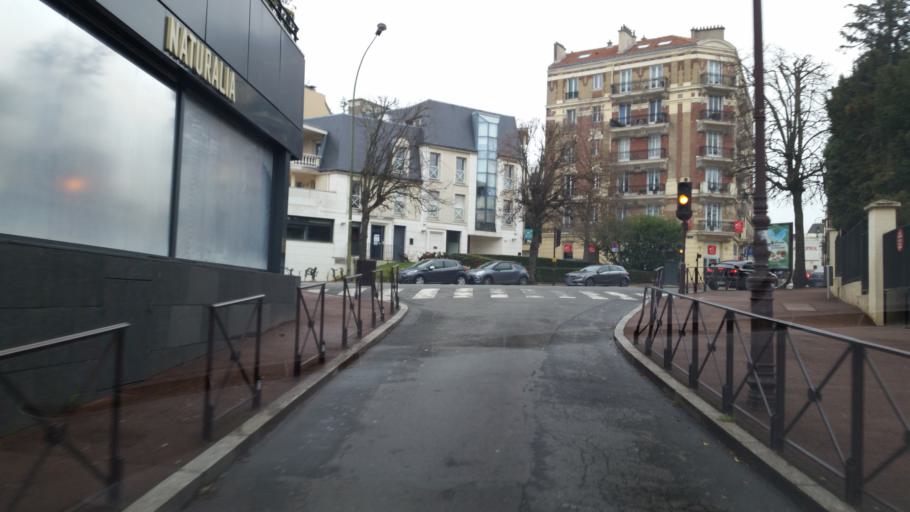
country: FR
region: Ile-de-France
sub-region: Departement des Hauts-de-Seine
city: Saint-Cloud
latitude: 48.8450
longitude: 2.2132
